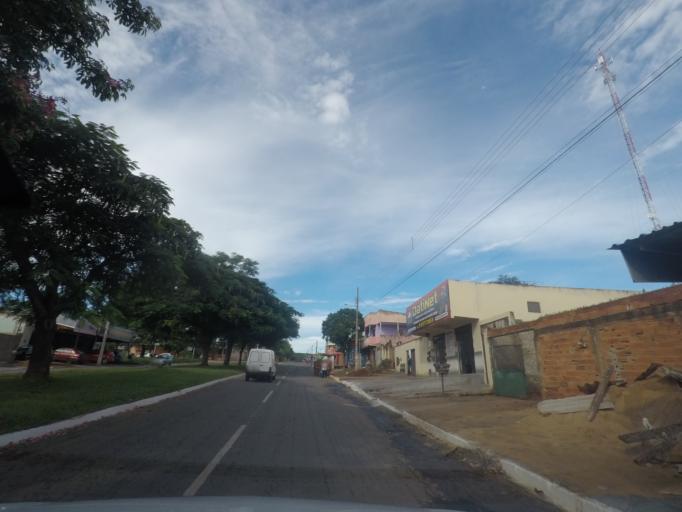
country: BR
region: Goias
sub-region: Aparecida De Goiania
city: Aparecida de Goiania
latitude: -16.8214
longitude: -49.3091
